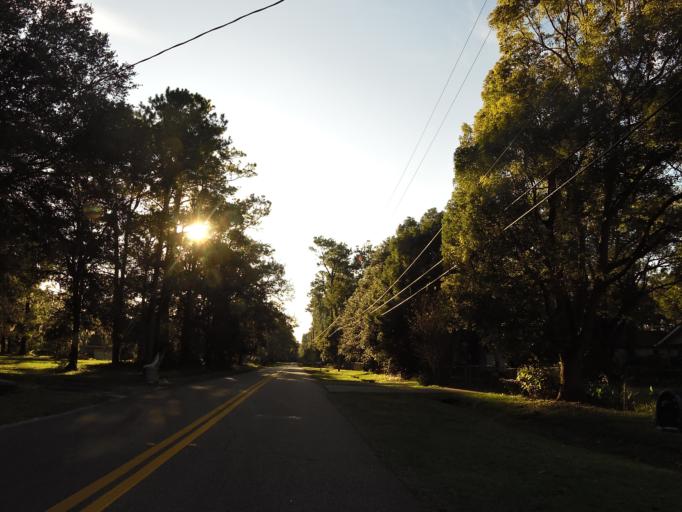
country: US
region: Florida
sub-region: Duval County
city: Jacksonville
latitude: 30.3654
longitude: -81.7493
